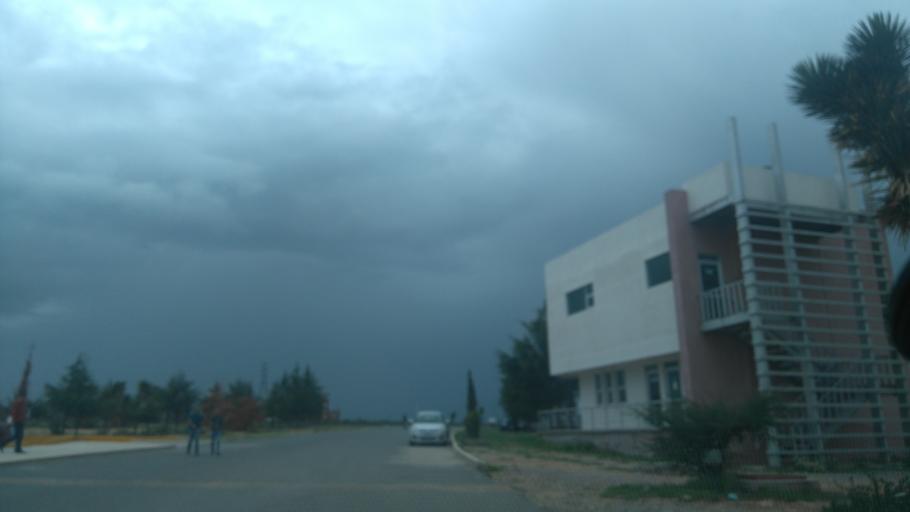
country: MX
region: Zacatecas
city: Zacatecas
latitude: 22.7710
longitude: -102.6437
